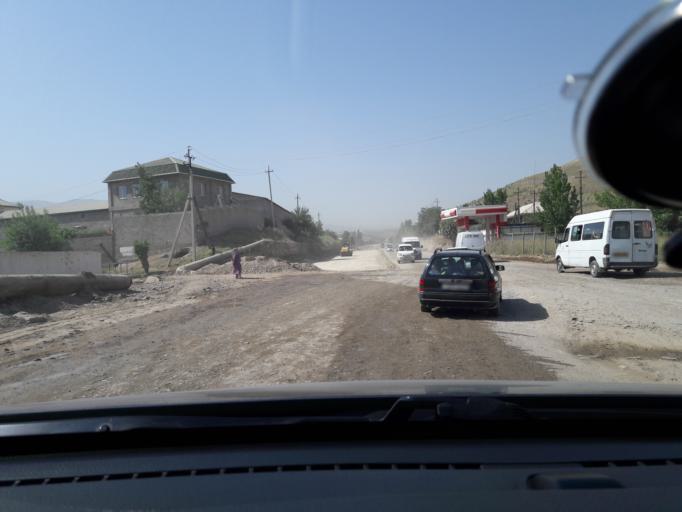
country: TJ
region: Dushanbe
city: Boshkengash
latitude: 38.4464
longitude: 68.7335
